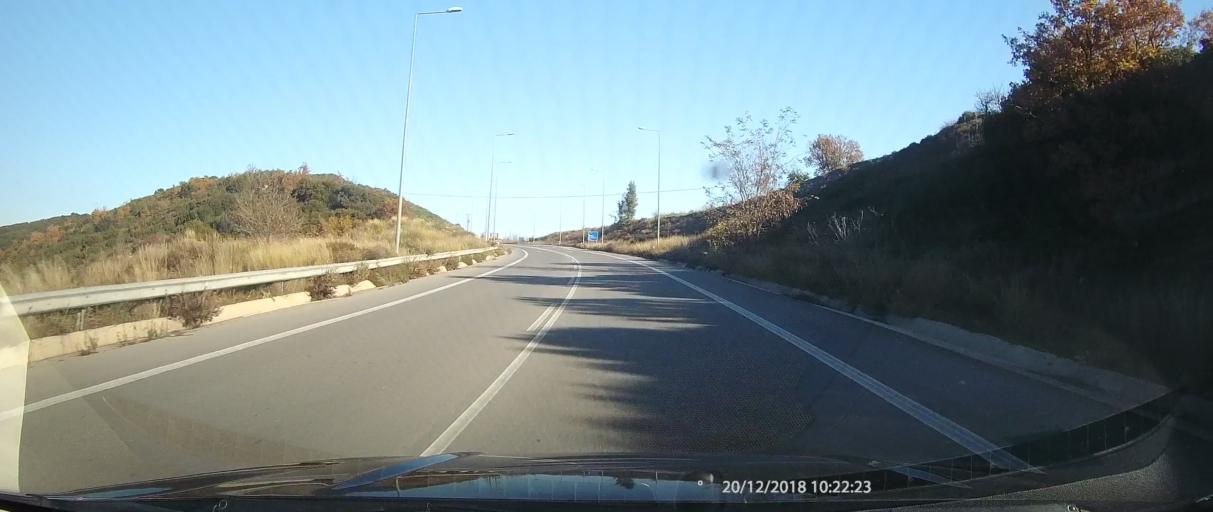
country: GR
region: Peloponnese
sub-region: Nomos Lakonias
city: Magoula
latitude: 37.1735
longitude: 22.4298
